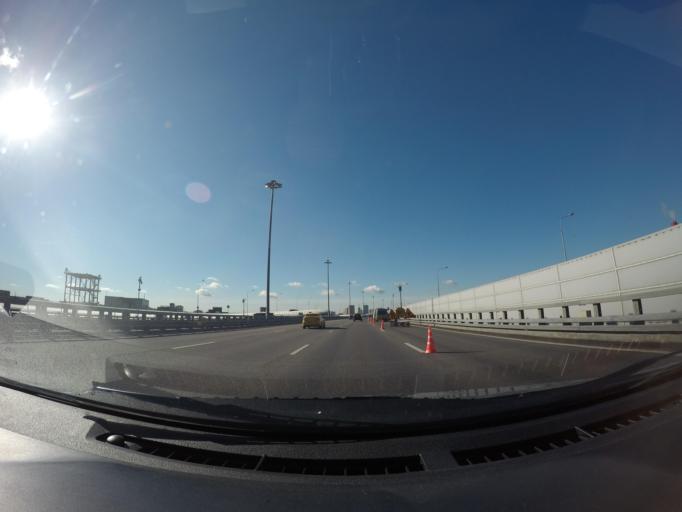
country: RU
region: Moscow
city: Ryazanskiy
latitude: 55.7553
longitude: 37.7468
